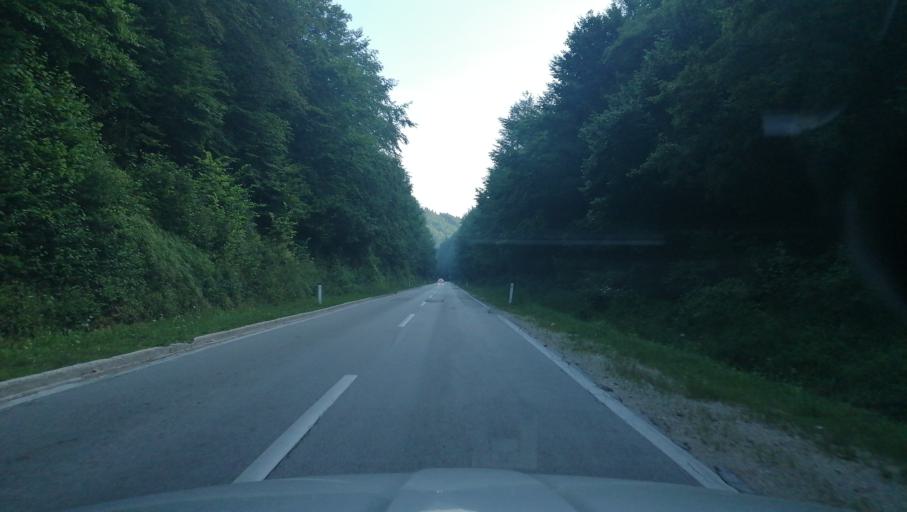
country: BA
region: Federation of Bosnia and Herzegovina
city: Gornji Vakuf
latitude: 43.8817
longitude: 17.5916
